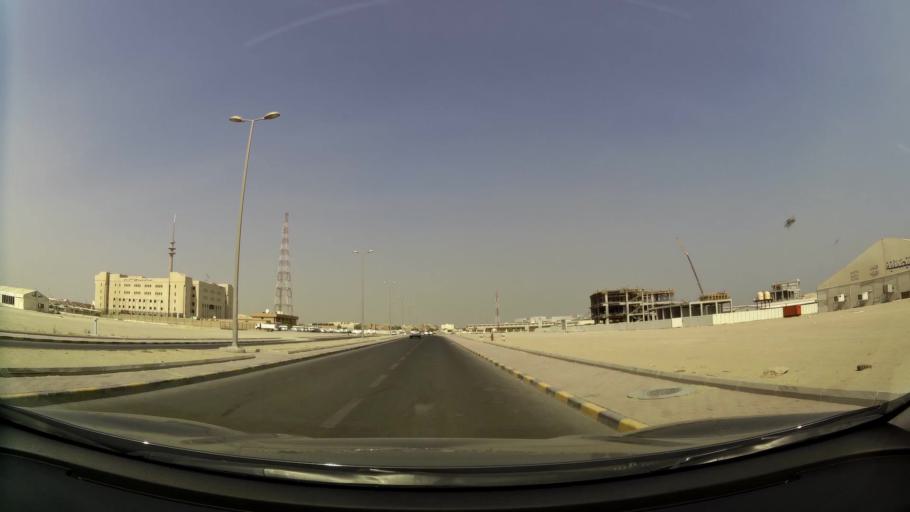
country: KW
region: Al Ahmadi
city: Al Fahahil
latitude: 29.0835
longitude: 48.1083
